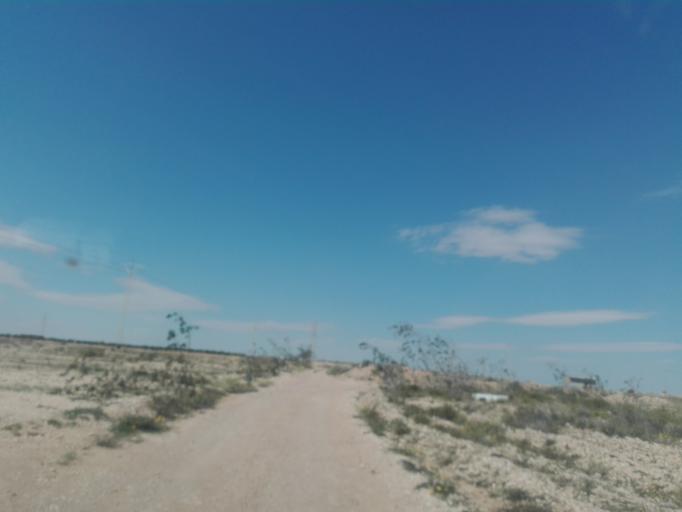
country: TN
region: Safaqis
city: Sfax
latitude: 34.6879
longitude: 10.5402
